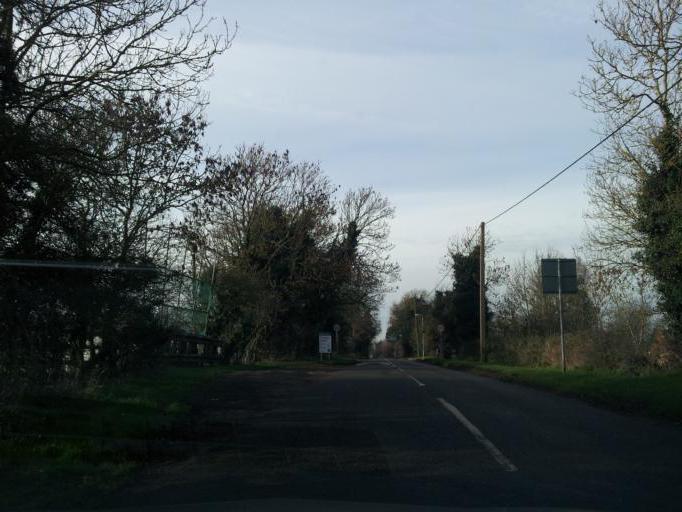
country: GB
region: England
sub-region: Northamptonshire
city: Blisworth
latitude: 52.1933
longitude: -0.9200
